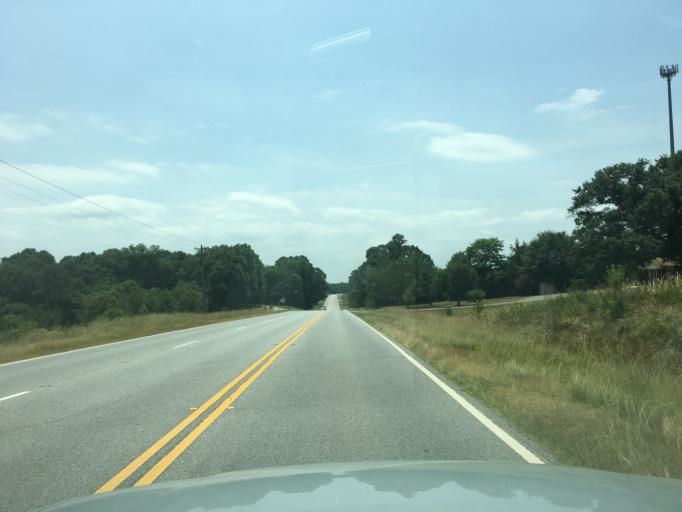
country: US
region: Georgia
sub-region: Hart County
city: Royston
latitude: 34.2752
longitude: -83.1654
